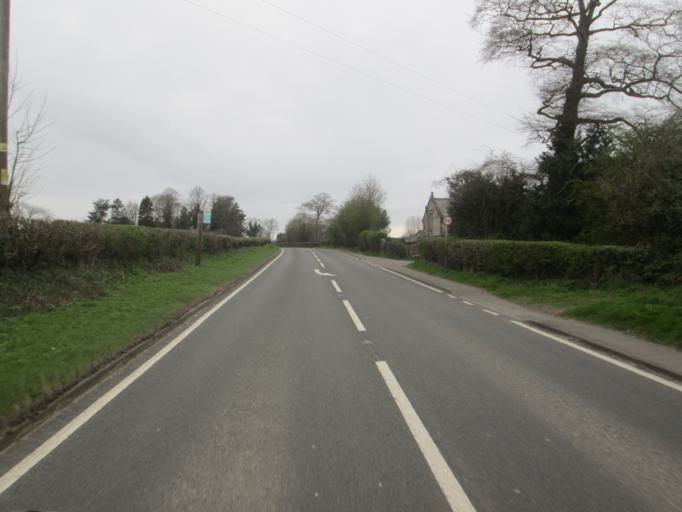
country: GB
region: England
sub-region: Derbyshire
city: Etwall
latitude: 52.9439
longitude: -1.5592
